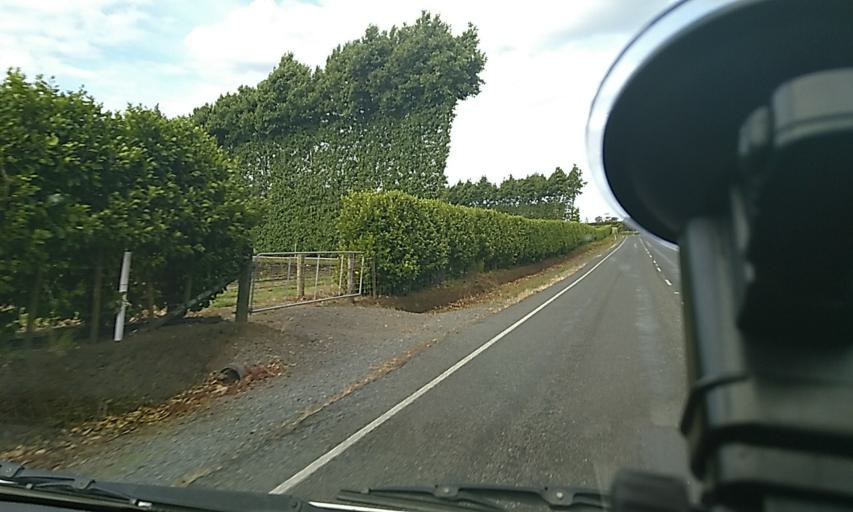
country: NZ
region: Bay of Plenty
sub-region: Western Bay of Plenty District
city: Waihi Beach
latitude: -37.4498
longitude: 175.9503
